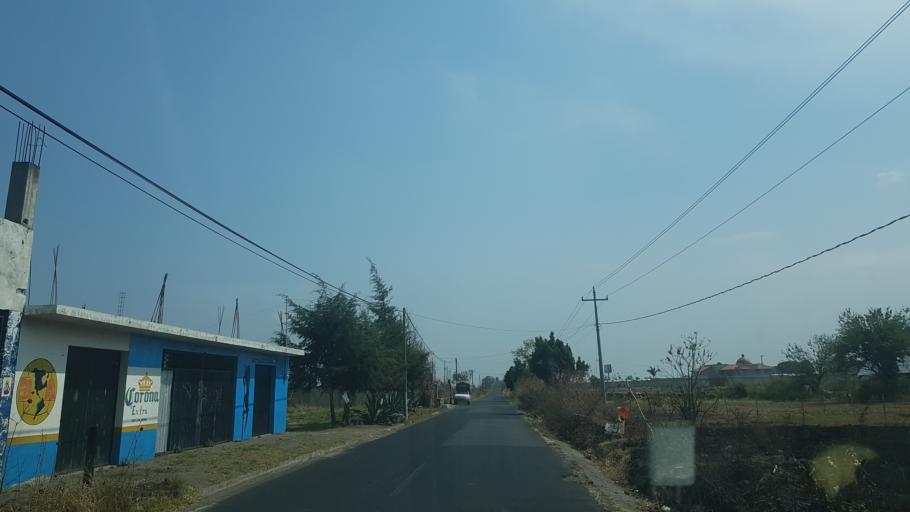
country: MX
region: Puebla
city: San Juan Tianguismanalco
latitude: 18.9400
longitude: -98.4541
